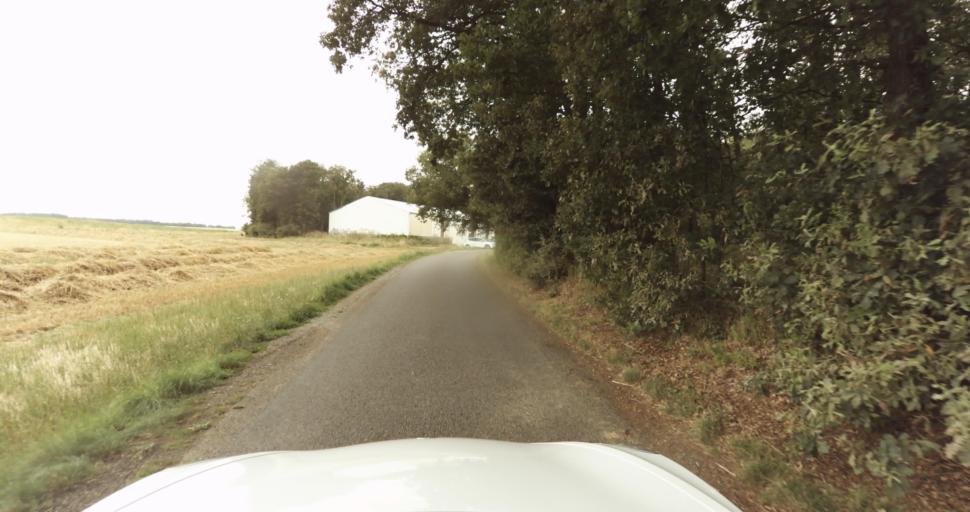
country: FR
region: Haute-Normandie
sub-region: Departement de l'Eure
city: Saint-Sebastien-de-Morsent
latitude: 49.0303
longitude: 1.0613
